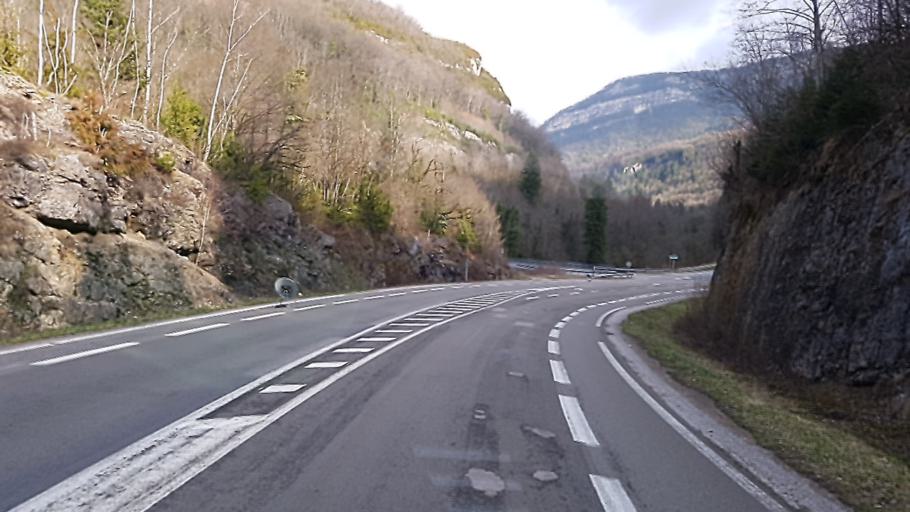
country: FR
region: Franche-Comte
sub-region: Departement du Jura
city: Lavans-les-Saint-Claude
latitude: 46.3817
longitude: 5.8021
